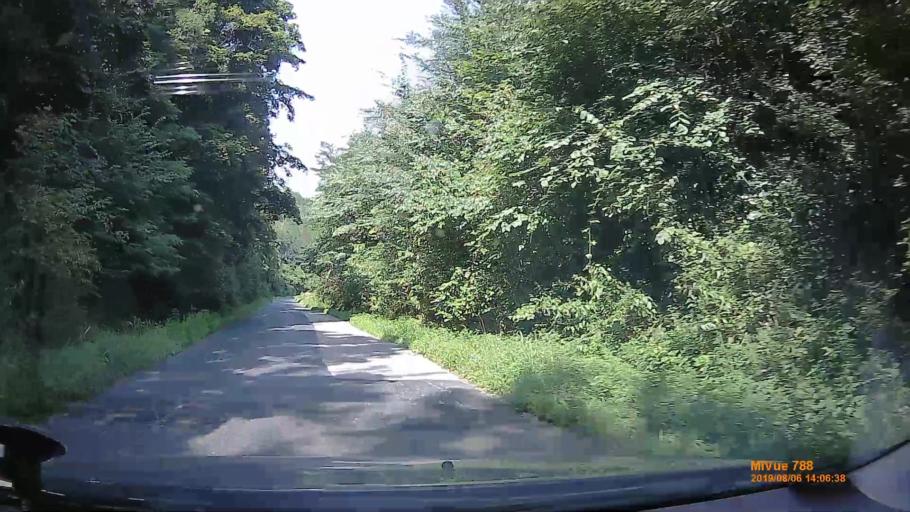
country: HU
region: Zala
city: Zalakomar
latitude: 46.5227
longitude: 17.0870
